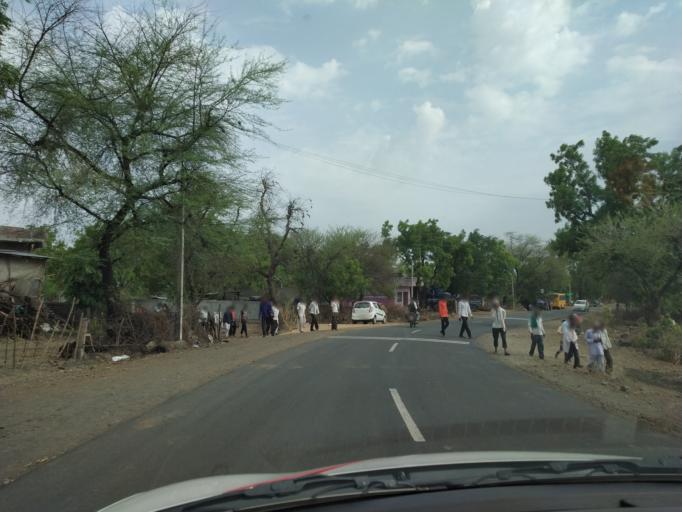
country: IN
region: Rajasthan
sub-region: Jhalawar
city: Bakani
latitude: 24.2303
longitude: 76.1657
